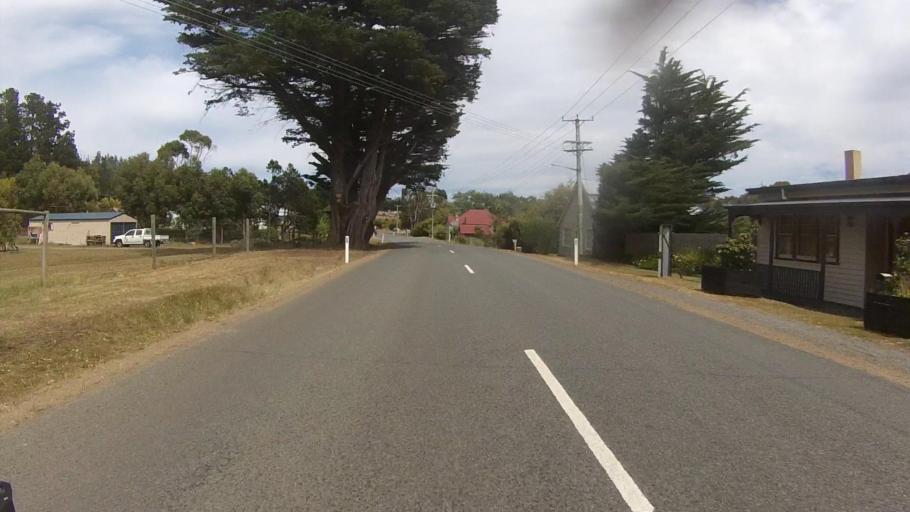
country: AU
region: Tasmania
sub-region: Sorell
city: Sorell
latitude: -42.8194
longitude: 147.8039
